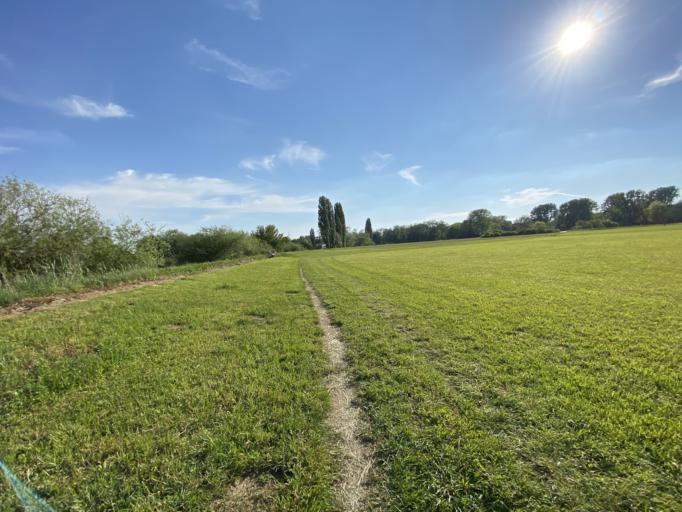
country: DE
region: Bavaria
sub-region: Regierungsbezirk Mittelfranken
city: Erlangen
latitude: 49.5909
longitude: 10.9859
